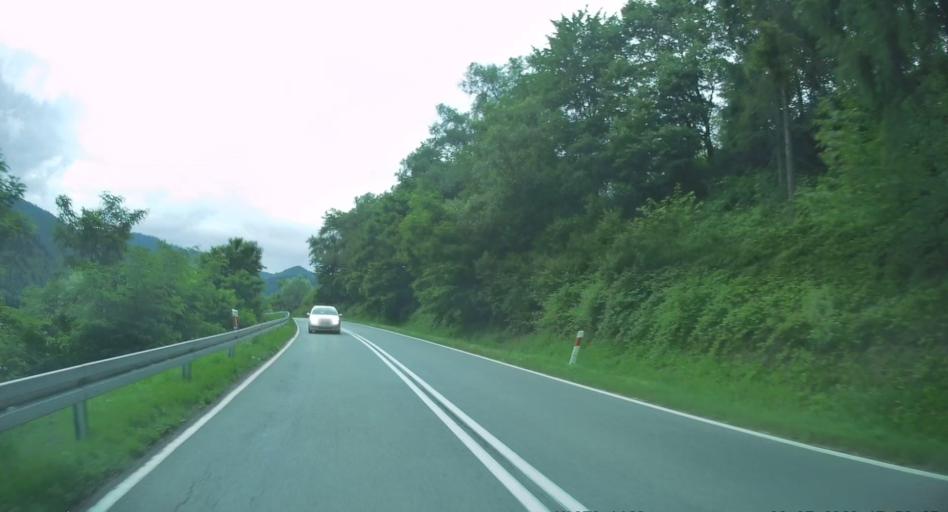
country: PL
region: Lesser Poland Voivodeship
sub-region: Powiat nowosadecki
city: Piwniczna-Zdroj
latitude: 49.3850
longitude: 20.7626
